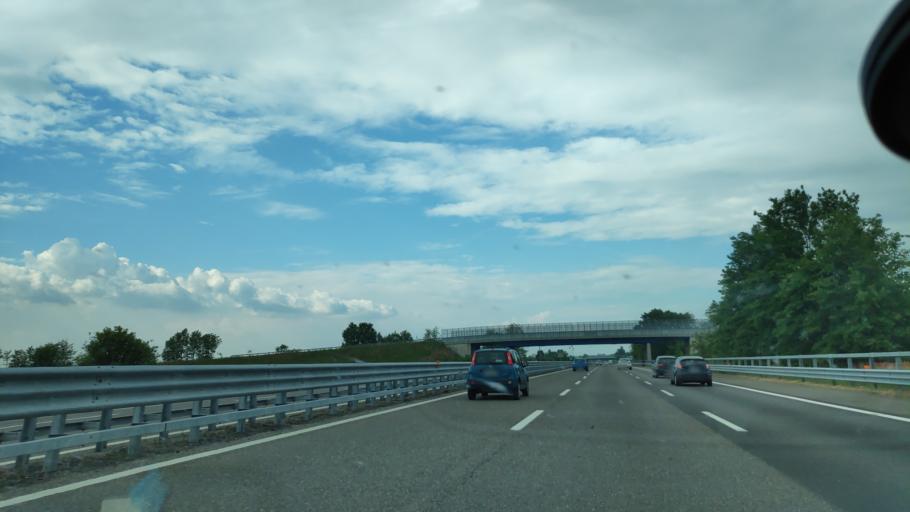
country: IT
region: Lombardy
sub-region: Provincia di Pavia
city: Pieve Albignola
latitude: 45.1362
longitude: 8.9842
